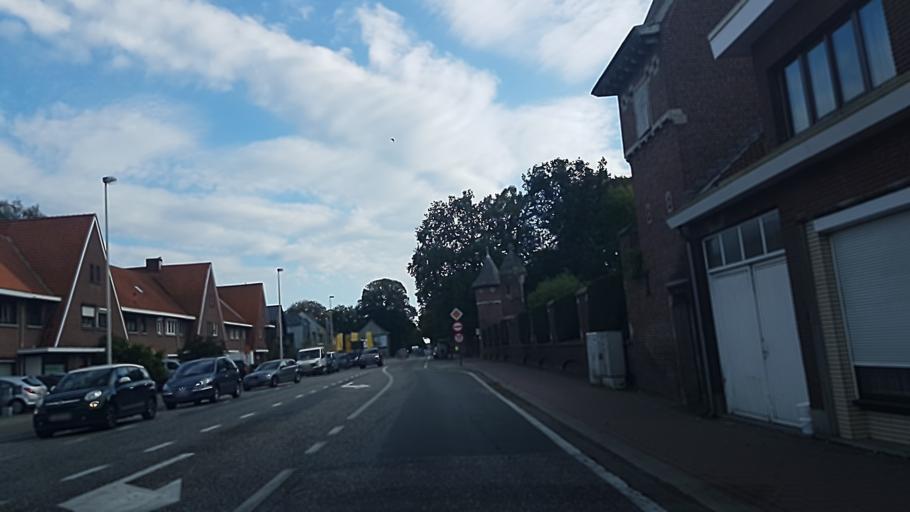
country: BE
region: Flanders
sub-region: Provincie Antwerpen
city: Kapellen
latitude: 51.3285
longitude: 4.4160
